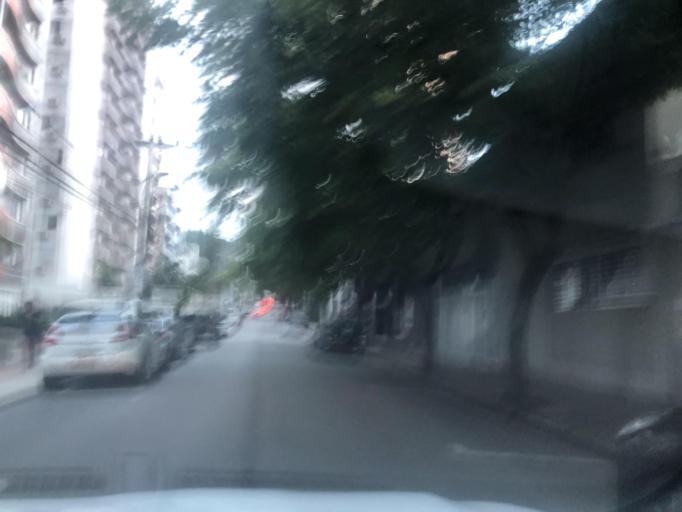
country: BR
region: Santa Catarina
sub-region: Florianopolis
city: Florianopolis
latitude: -27.5910
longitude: -48.5483
